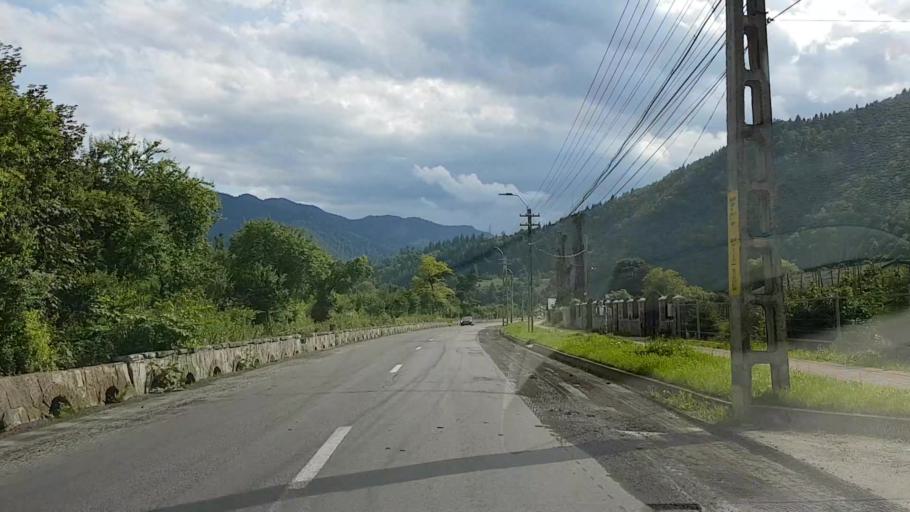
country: RO
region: Neamt
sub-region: Comuna Bicaz
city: Dodeni
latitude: 46.9245
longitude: 26.0927
